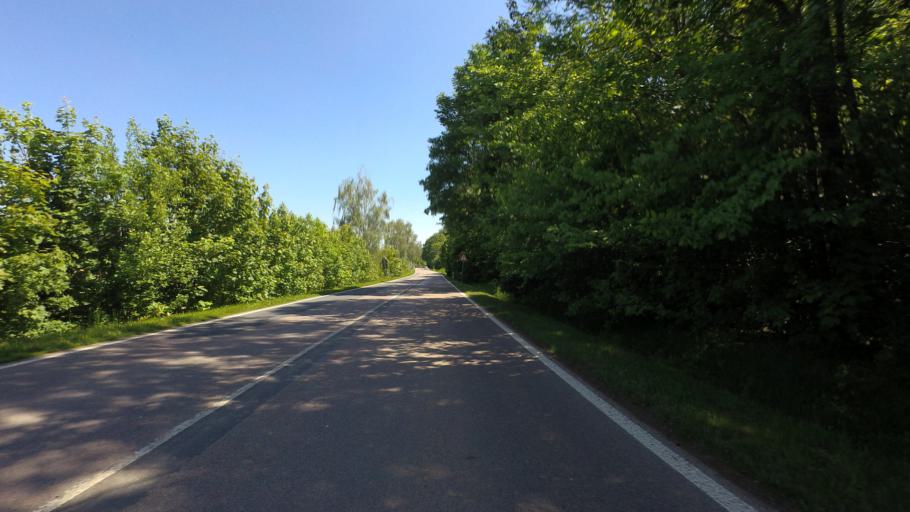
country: DE
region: Saxony
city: Klipphausen
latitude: 51.1179
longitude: 13.5479
